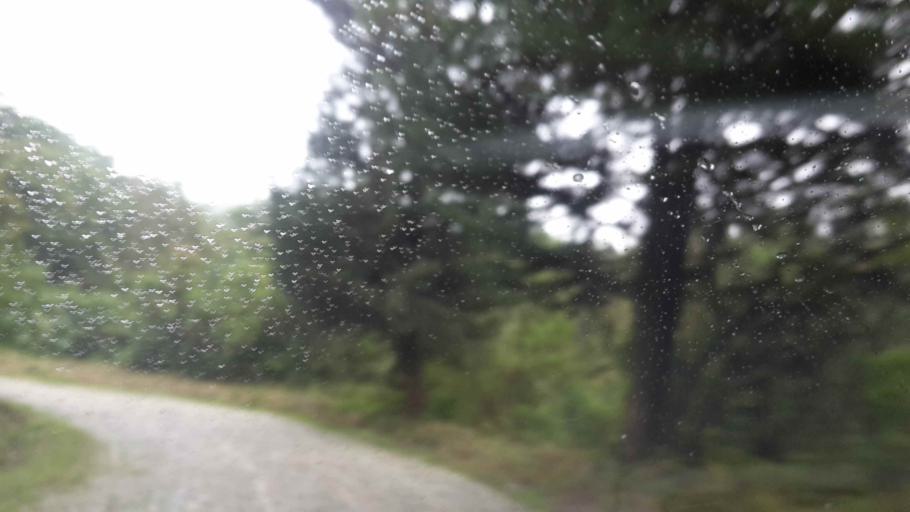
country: BO
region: Cochabamba
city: Colomi
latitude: -17.1626
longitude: -65.9006
